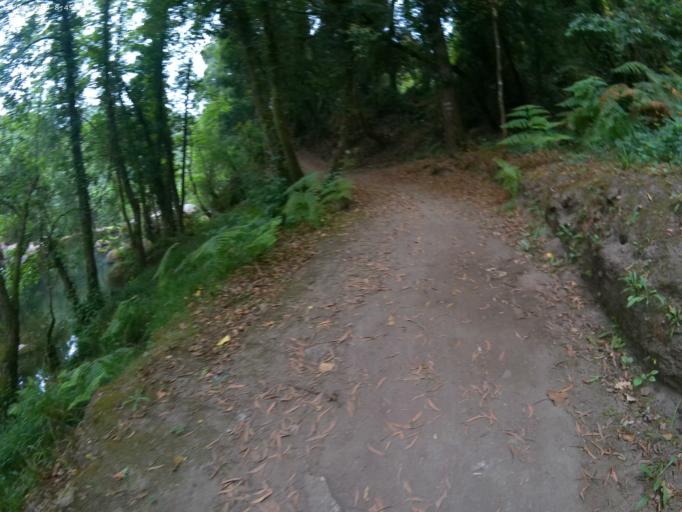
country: PT
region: Viana do Castelo
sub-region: Ponte da Barca
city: Ponte da Barca
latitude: 41.8103
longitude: -8.4301
